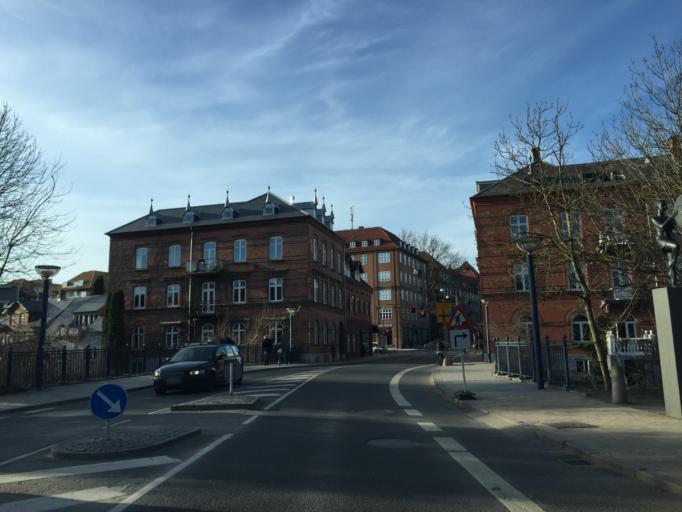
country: DK
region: South Denmark
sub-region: Odense Kommune
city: Odense
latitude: 55.3922
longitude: 10.3871
